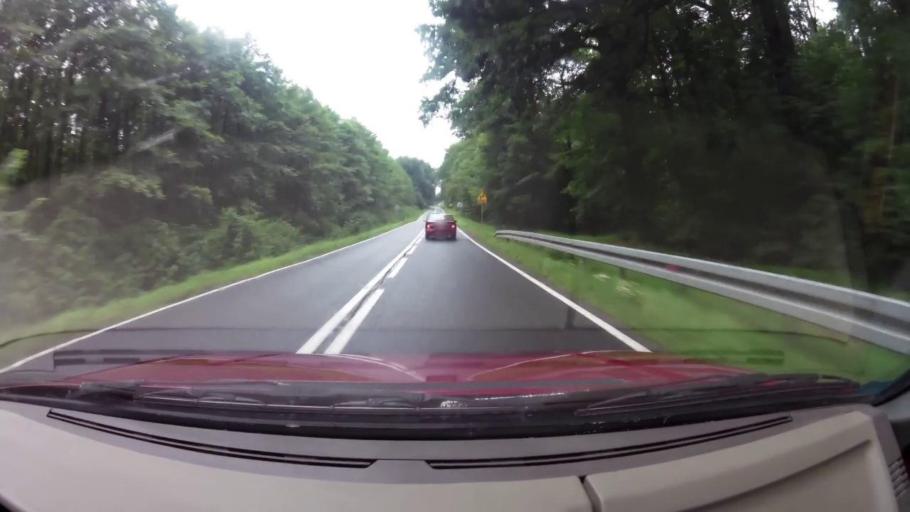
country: PL
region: West Pomeranian Voivodeship
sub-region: Powiat stargardzki
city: Marianowo
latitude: 53.4191
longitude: 15.2716
